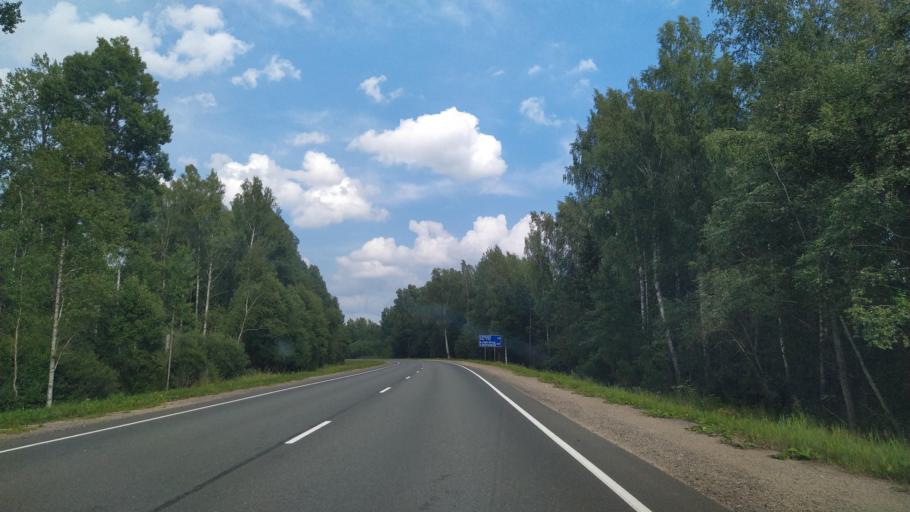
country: RU
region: Pskov
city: Dno
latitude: 57.9963
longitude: 29.8673
